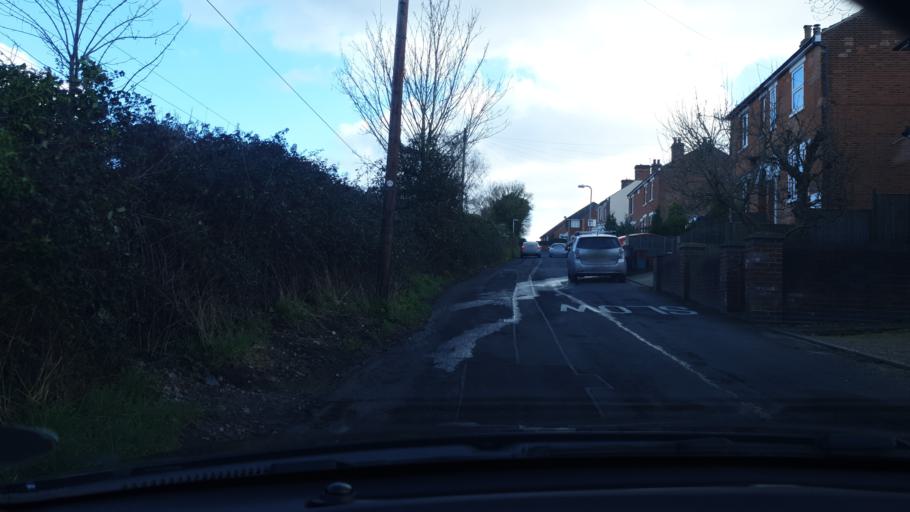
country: GB
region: England
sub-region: Essex
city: Manningtree
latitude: 51.9431
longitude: 1.0616
